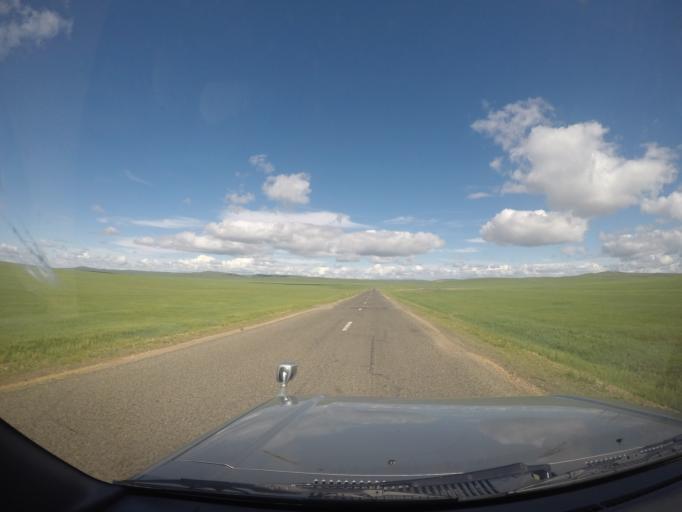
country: MN
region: Hentiy
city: Bayanbulag
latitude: 47.4598
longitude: 109.6486
